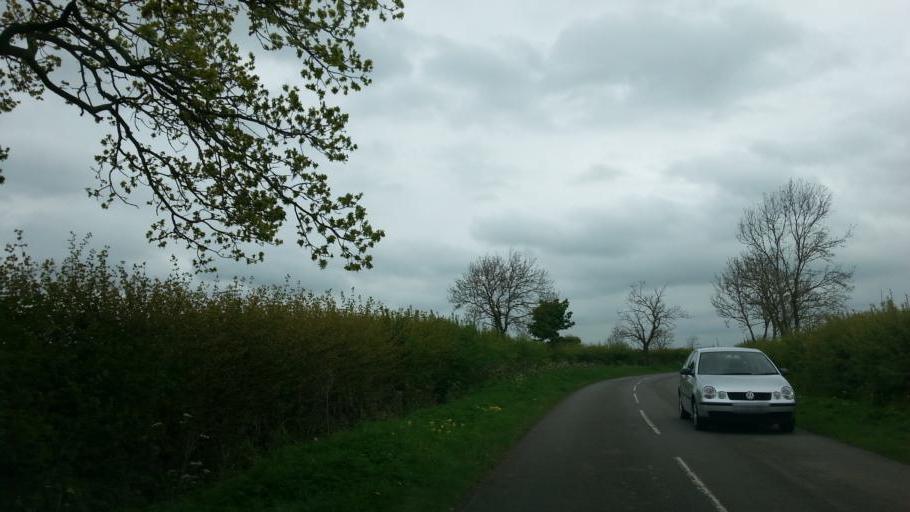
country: GB
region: England
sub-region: Lincolnshire
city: Grantham
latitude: 52.8657
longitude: -0.5183
